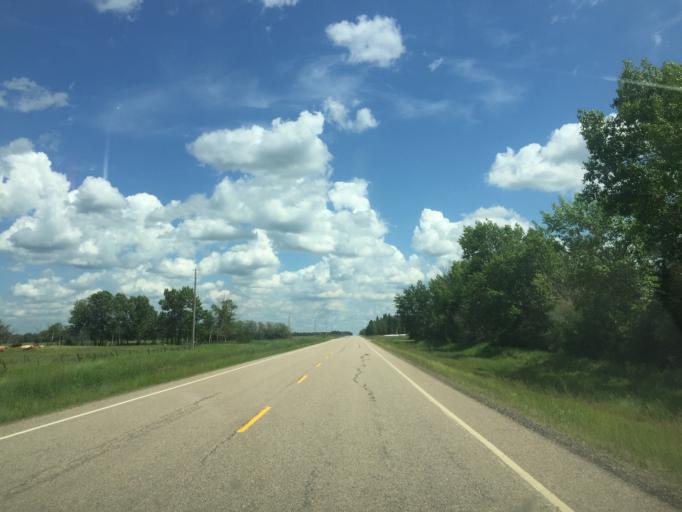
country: CA
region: Alberta
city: Athabasca
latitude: 54.3267
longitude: -113.3154
